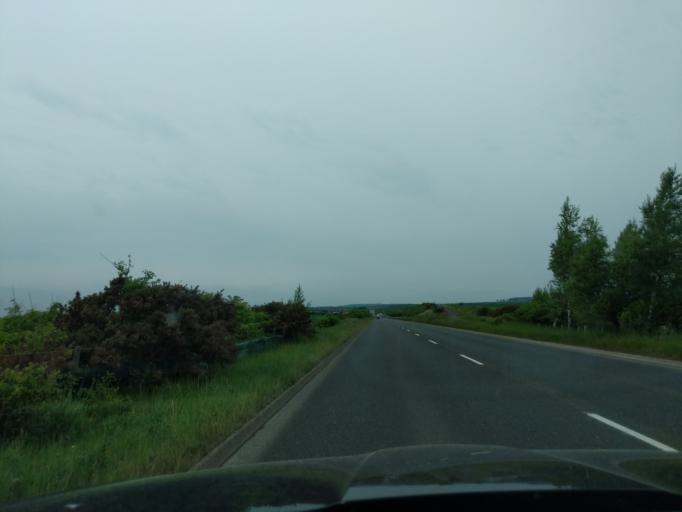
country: GB
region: England
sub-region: Northumberland
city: Pegswood
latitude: 55.1763
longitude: -1.6609
